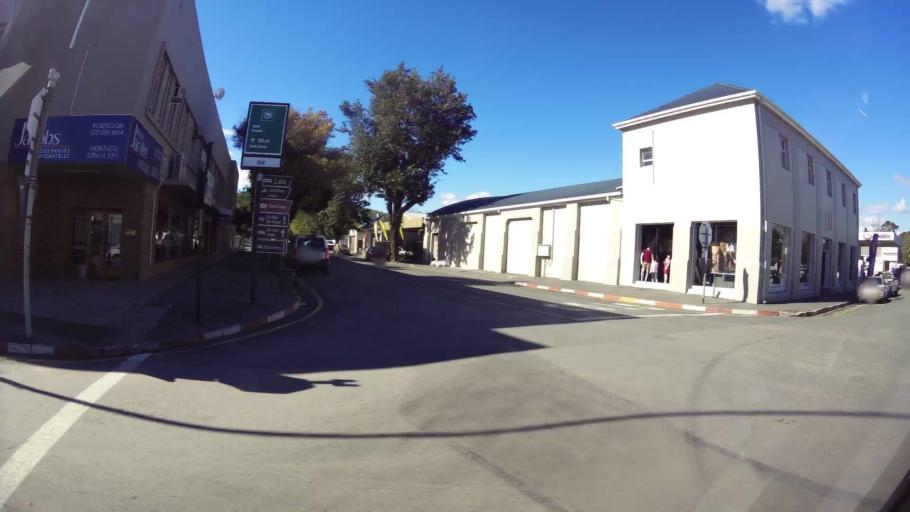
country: ZA
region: Western Cape
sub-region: Cape Winelands District Municipality
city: Ashton
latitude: -33.8055
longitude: 19.8836
